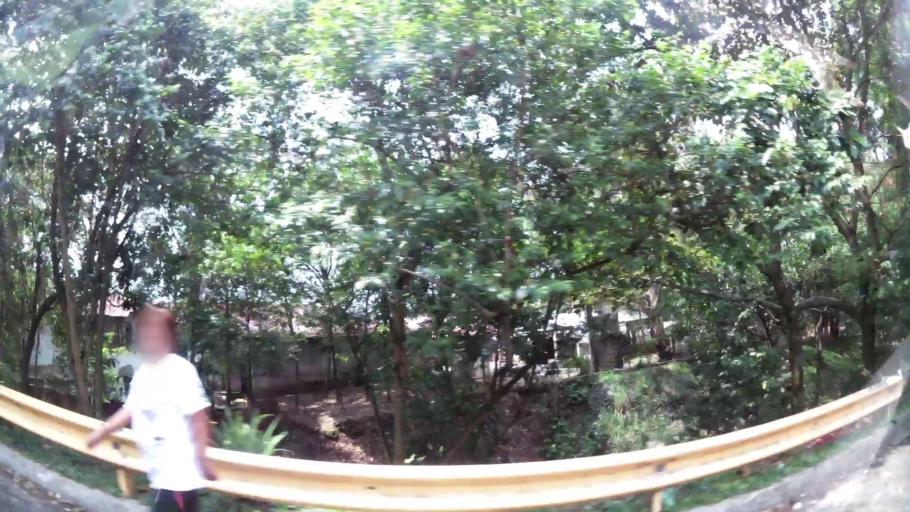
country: CO
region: Antioquia
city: Medellin
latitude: 6.2621
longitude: -75.5497
